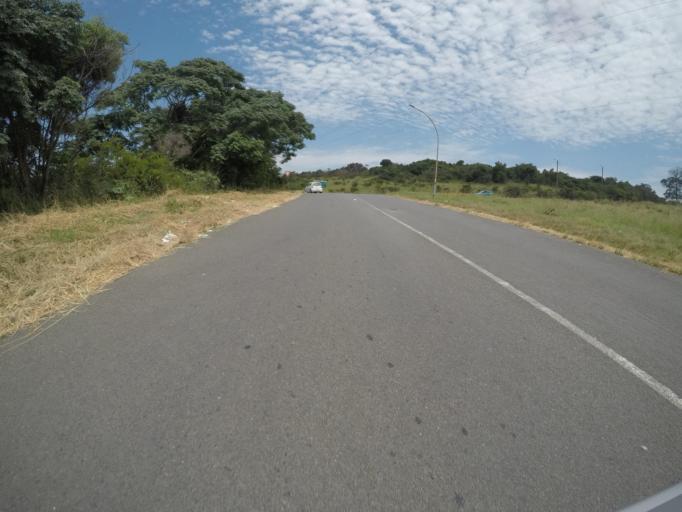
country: ZA
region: Eastern Cape
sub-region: Buffalo City Metropolitan Municipality
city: East London
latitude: -32.9822
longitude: 27.8705
